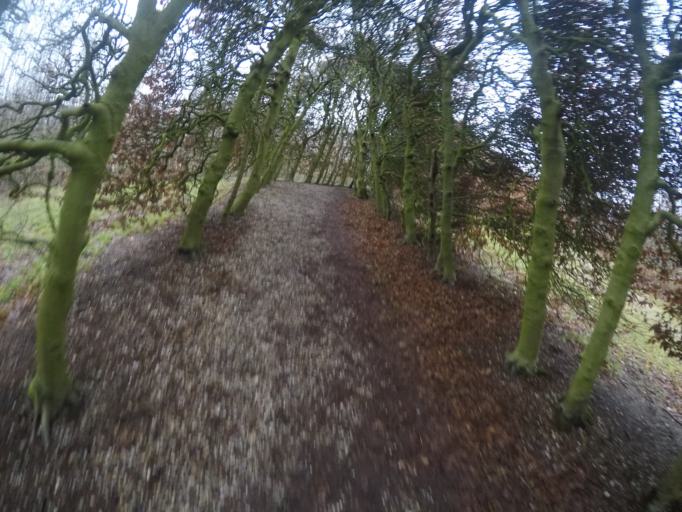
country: NL
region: Gelderland
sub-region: Gemeente Arnhem
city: Hoogkamp
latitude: 51.9929
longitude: 5.8658
